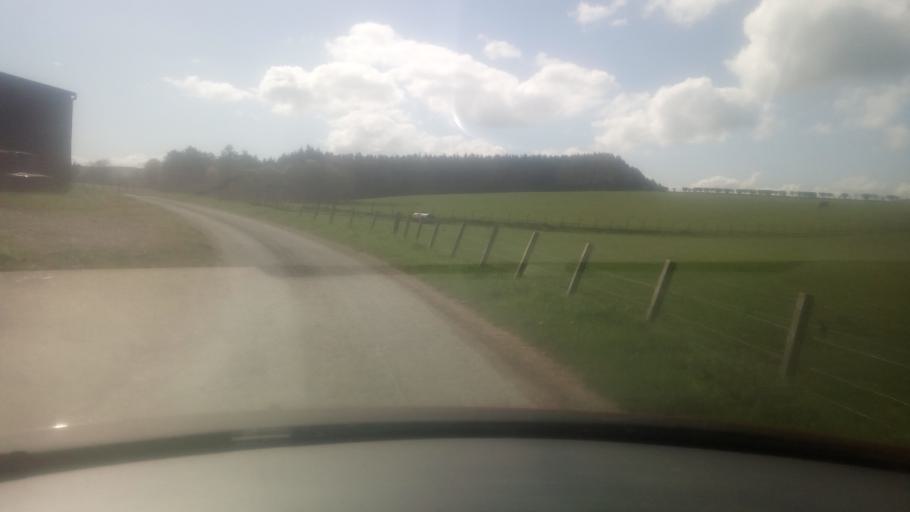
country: GB
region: Scotland
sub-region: The Scottish Borders
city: Hawick
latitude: 55.4286
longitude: -2.7035
